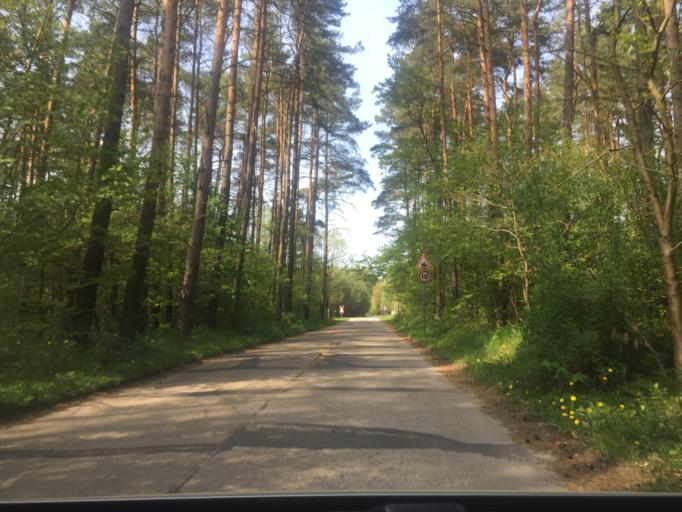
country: DE
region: Mecklenburg-Vorpommern
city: Torgelow
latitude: 53.6255
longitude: 13.9884
